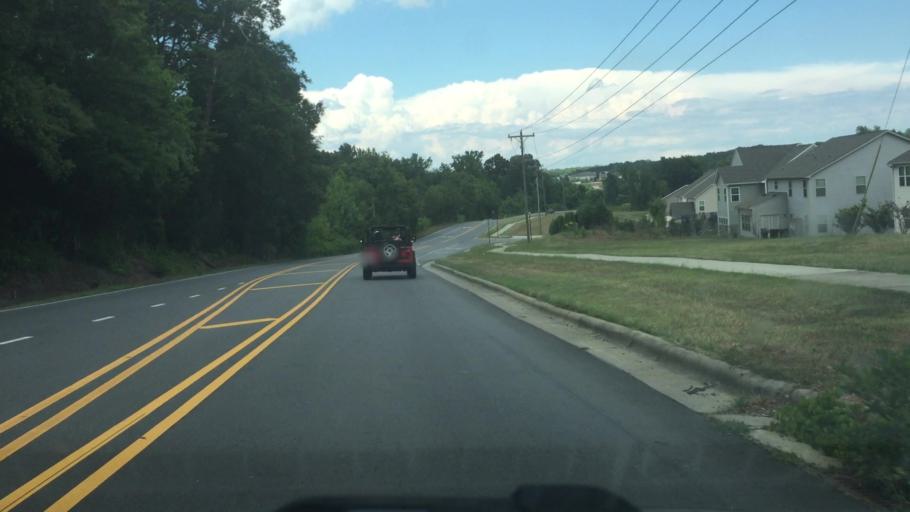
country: US
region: North Carolina
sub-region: Mecklenburg County
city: Huntersville
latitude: 35.4208
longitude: -80.7439
